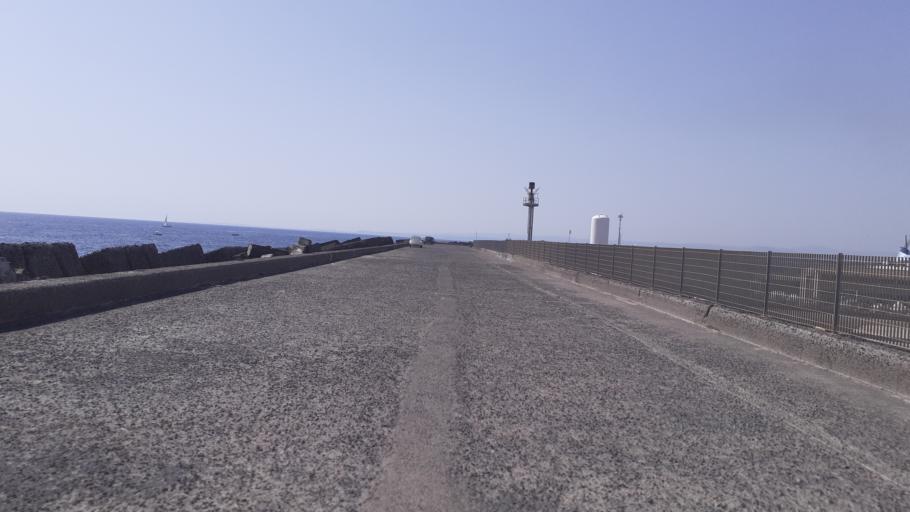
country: IT
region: Sicily
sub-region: Catania
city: Catania
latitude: 37.4929
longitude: 15.0999
